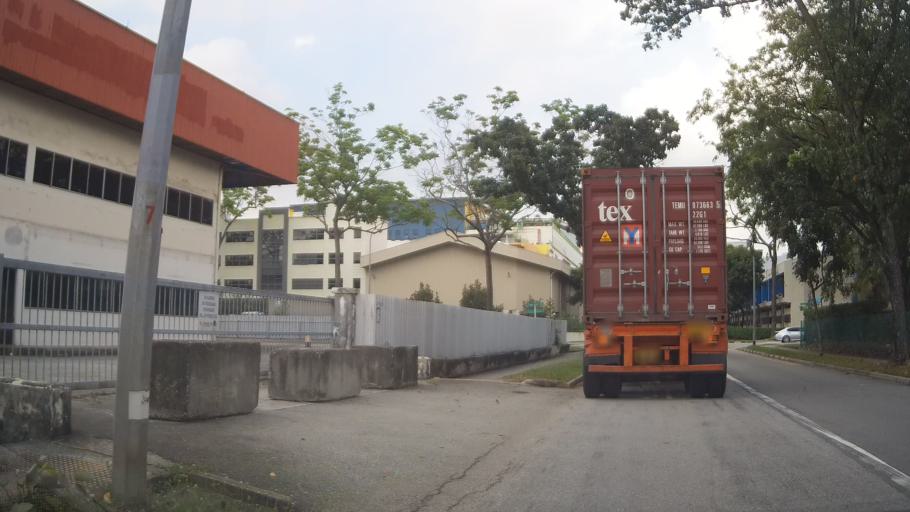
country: MY
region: Johor
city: Johor Bahru
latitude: 1.3224
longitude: 103.6414
